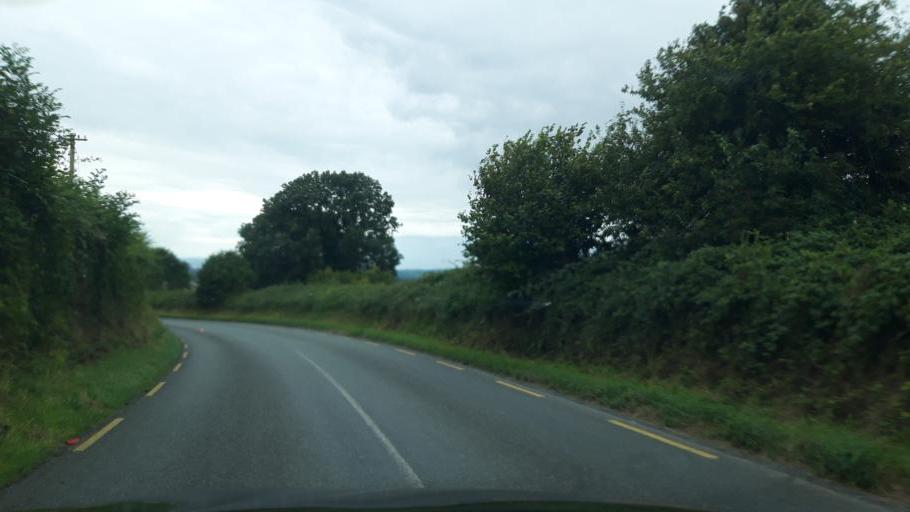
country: IE
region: Leinster
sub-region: Kilkenny
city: Ballyragget
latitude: 52.7949
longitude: -7.3172
